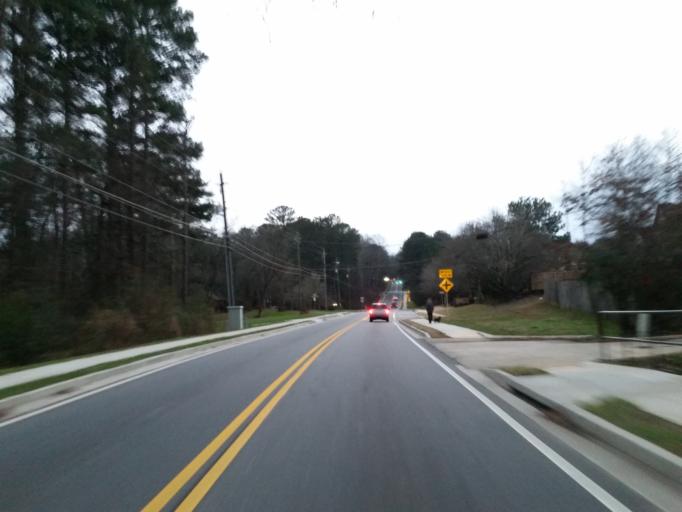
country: US
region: Georgia
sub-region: Cobb County
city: Mableton
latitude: 33.8527
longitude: -84.5781
